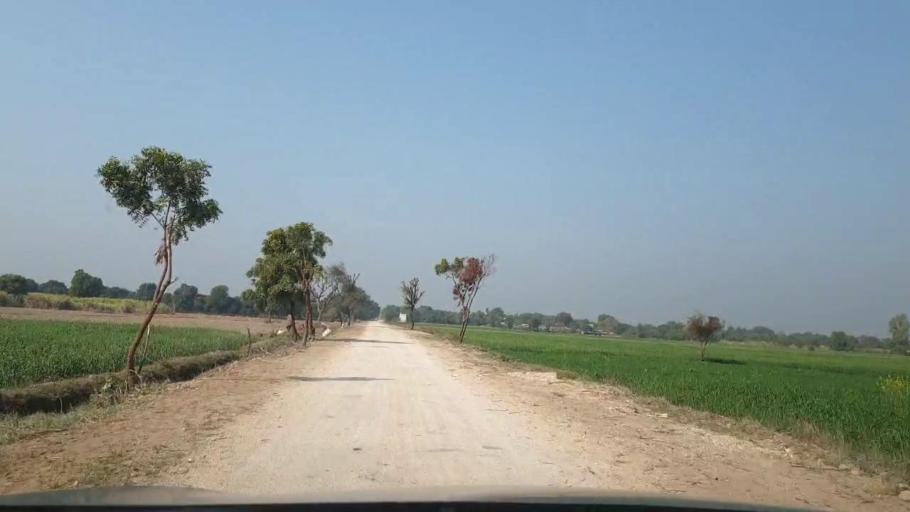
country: PK
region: Sindh
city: Tando Allahyar
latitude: 25.5180
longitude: 68.7586
